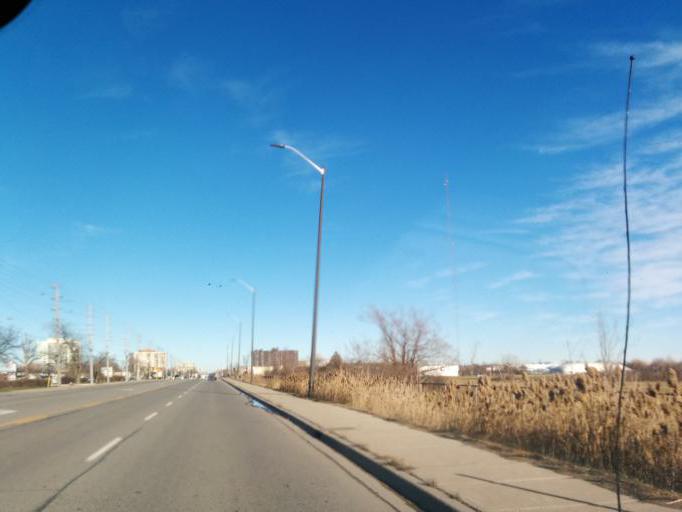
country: CA
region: Ontario
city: Oakville
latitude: 43.5054
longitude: -79.6360
